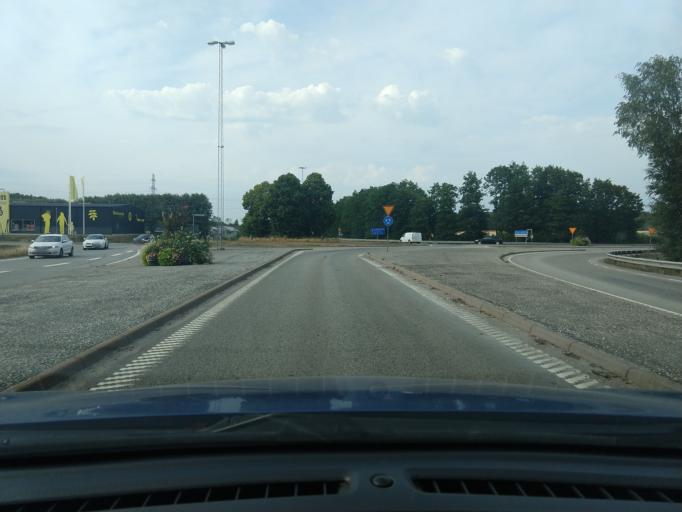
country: SE
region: Blekinge
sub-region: Ronneby Kommun
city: Kallinge
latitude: 56.2322
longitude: 15.2600
